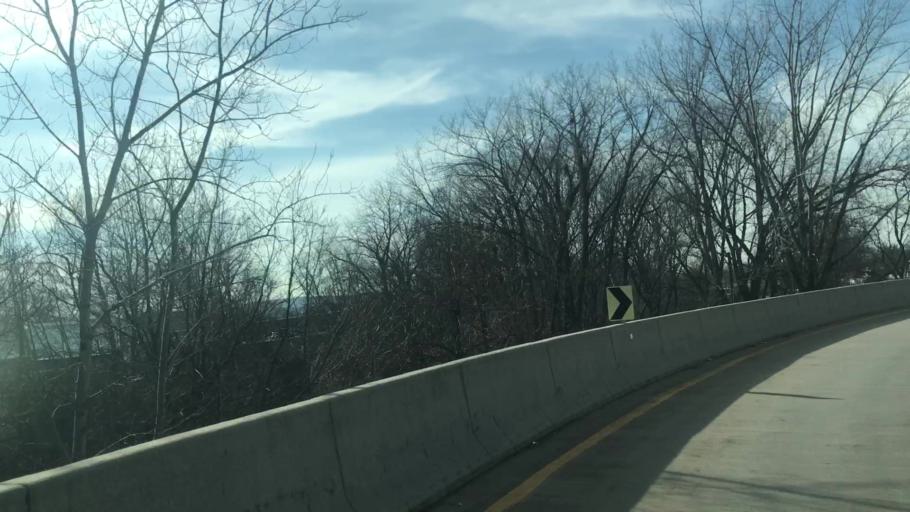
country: US
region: New Jersey
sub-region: Bergen County
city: Elmwood Park
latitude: 40.9026
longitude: -74.1114
